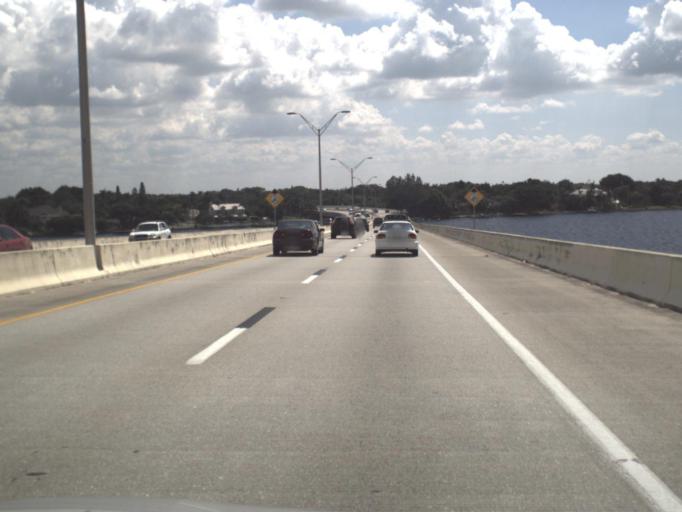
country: US
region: Florida
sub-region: Lee County
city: Whiskey Creek
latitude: 26.5997
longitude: -81.8991
